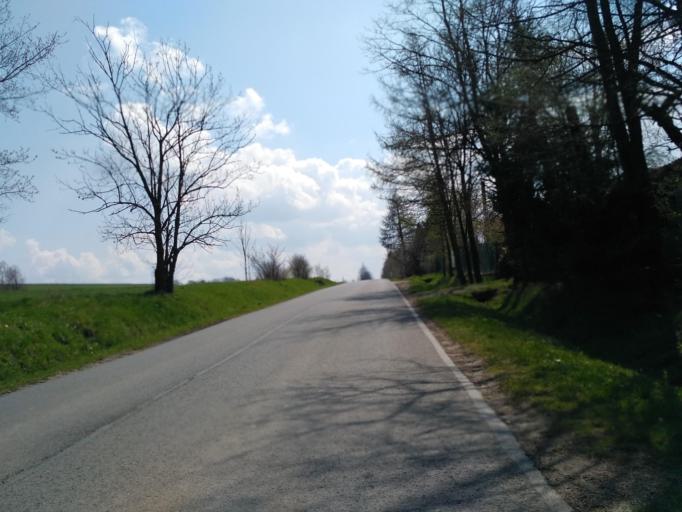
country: PL
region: Subcarpathian Voivodeship
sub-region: Powiat sanocki
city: Bukowsko
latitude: 49.5000
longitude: 22.0374
